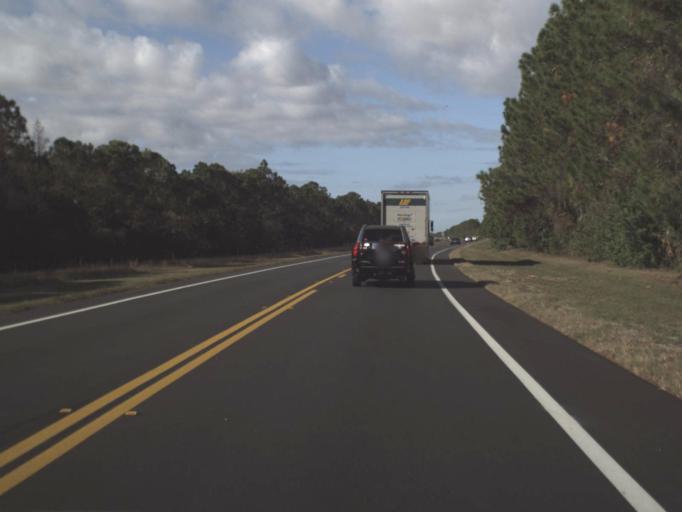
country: US
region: Florida
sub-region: Volusia County
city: South Daytona
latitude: 29.1416
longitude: -81.0579
